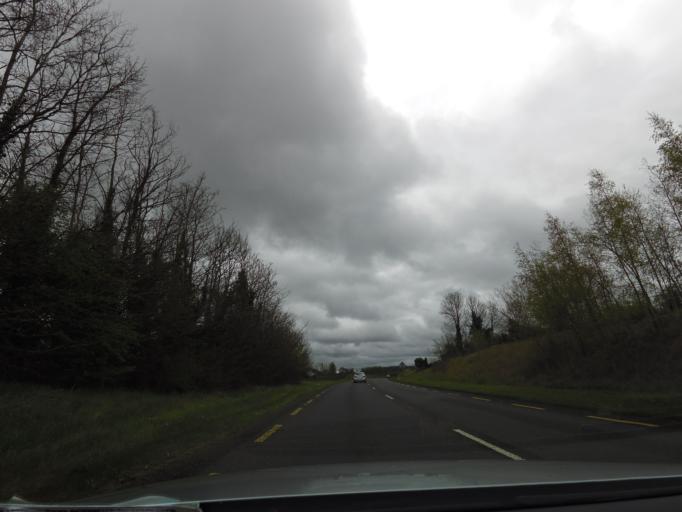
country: IE
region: Leinster
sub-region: Kilkenny
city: Ballyragget
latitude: 52.7160
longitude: -7.3325
